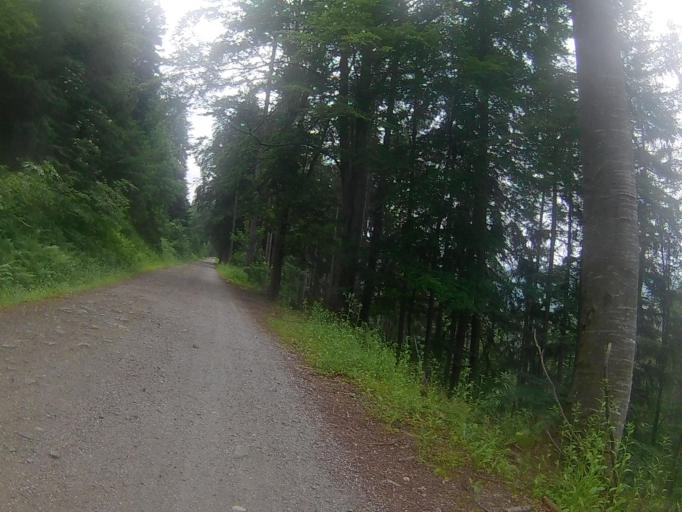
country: SI
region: Ruse
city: Ruse
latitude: 46.5188
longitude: 15.5366
